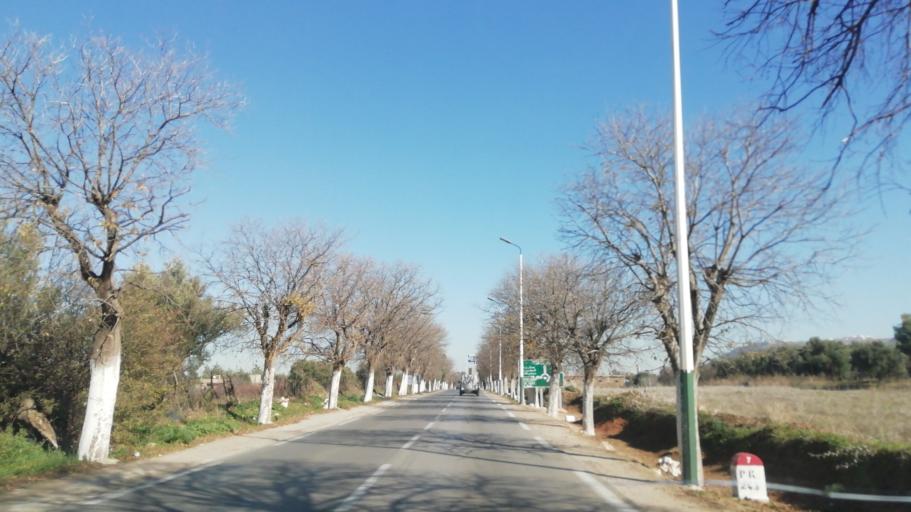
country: DZ
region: Tlemcen
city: Mansoura
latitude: 34.8658
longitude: -1.3520
